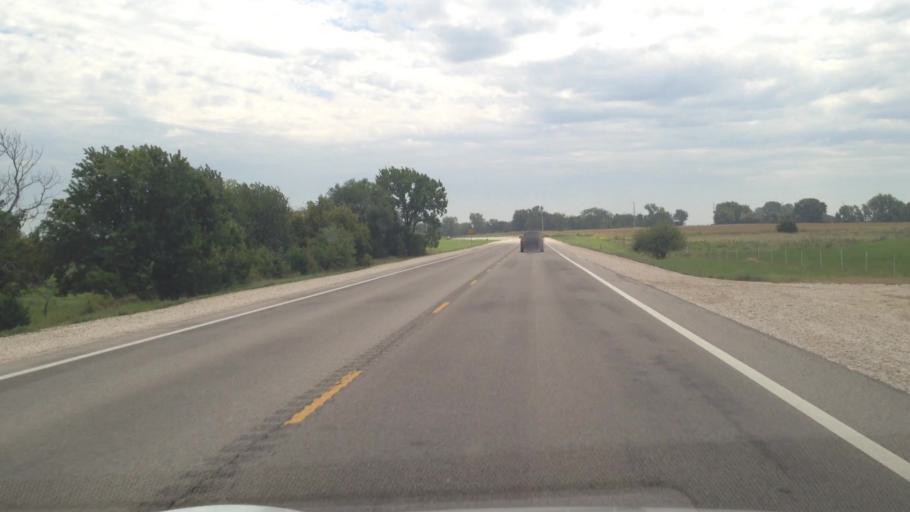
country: US
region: Kansas
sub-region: Allen County
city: Iola
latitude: 37.9186
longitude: -95.1557
